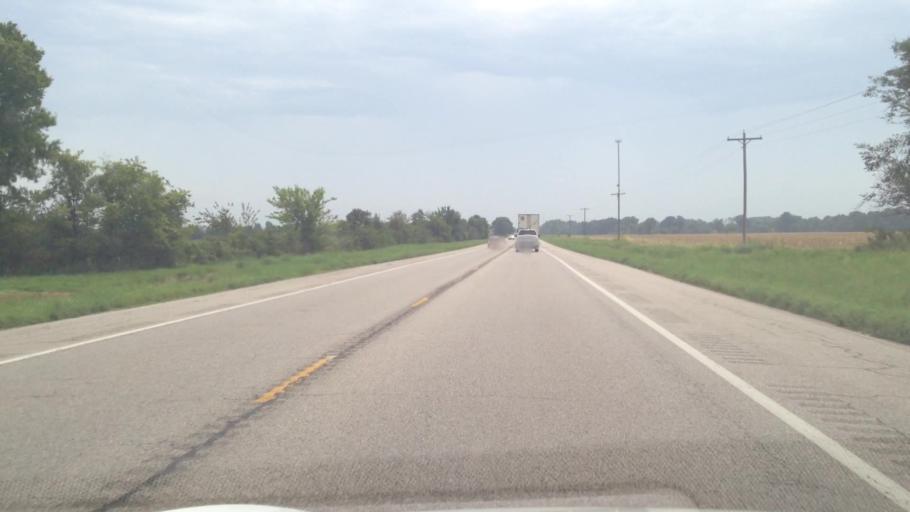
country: US
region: Missouri
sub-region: Jasper County
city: Carl Junction
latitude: 37.2151
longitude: -94.7049
